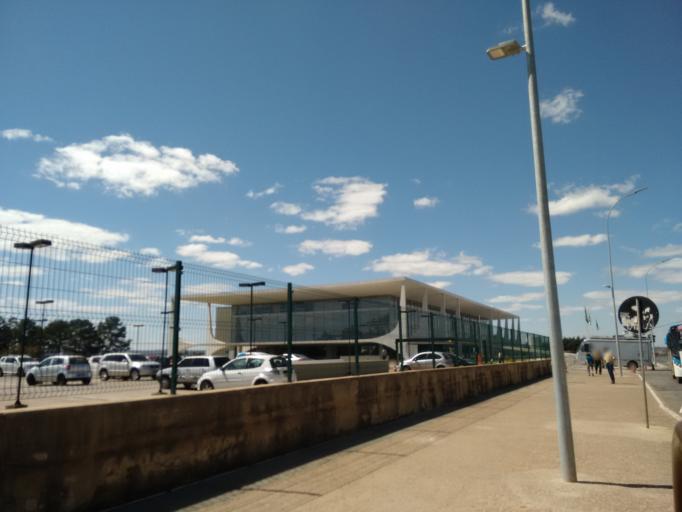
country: BR
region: Federal District
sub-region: Brasilia
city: Brasilia
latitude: -15.7991
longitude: -47.8623
